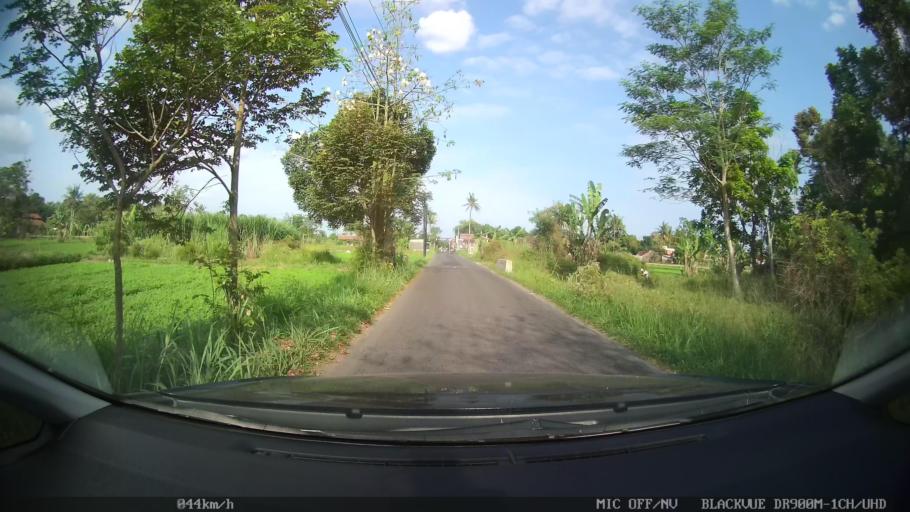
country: ID
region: Daerah Istimewa Yogyakarta
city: Depok
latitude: -7.7274
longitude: 110.4457
